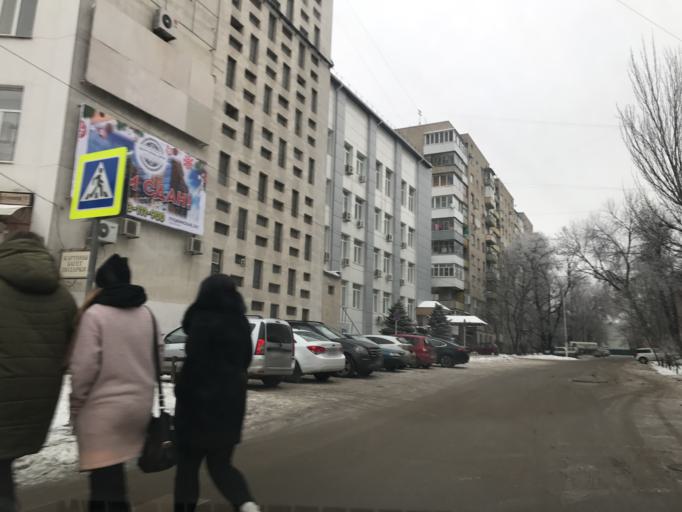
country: RU
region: Rostov
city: Rostov-na-Donu
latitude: 47.2324
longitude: 39.7024
